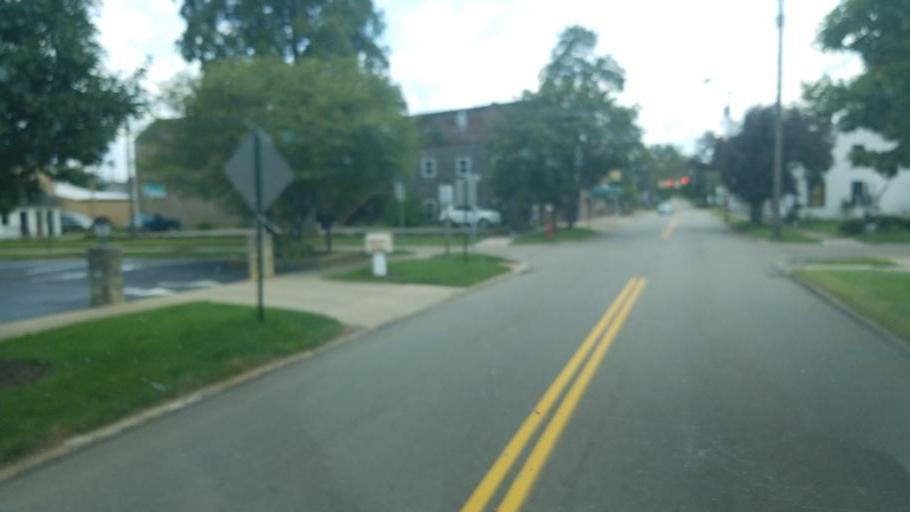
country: US
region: Ohio
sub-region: Carroll County
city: Lake Mohawk
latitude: 40.6525
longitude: -81.2987
